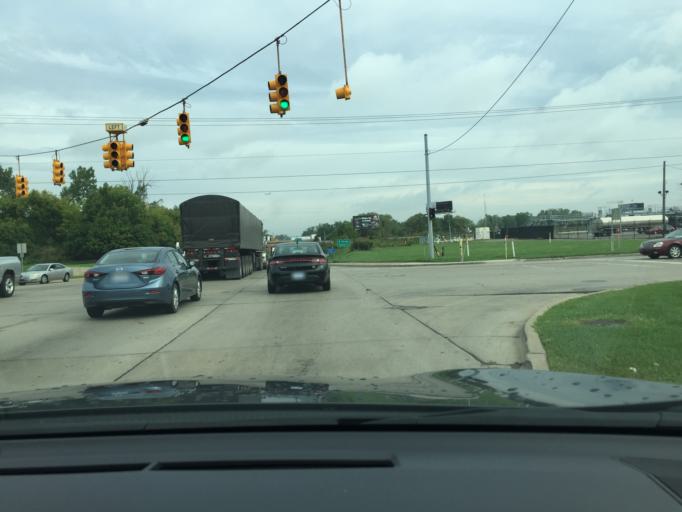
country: US
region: Michigan
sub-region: Wayne County
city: Taylor
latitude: 42.2387
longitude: -83.3277
